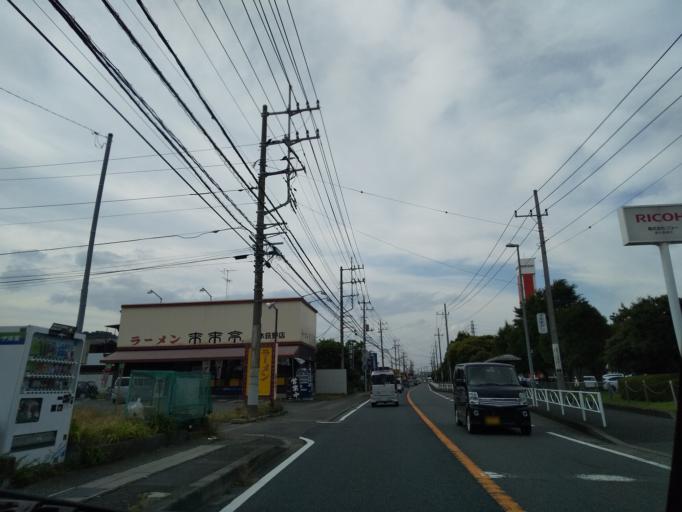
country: JP
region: Kanagawa
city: Zama
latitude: 35.4879
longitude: 139.3403
